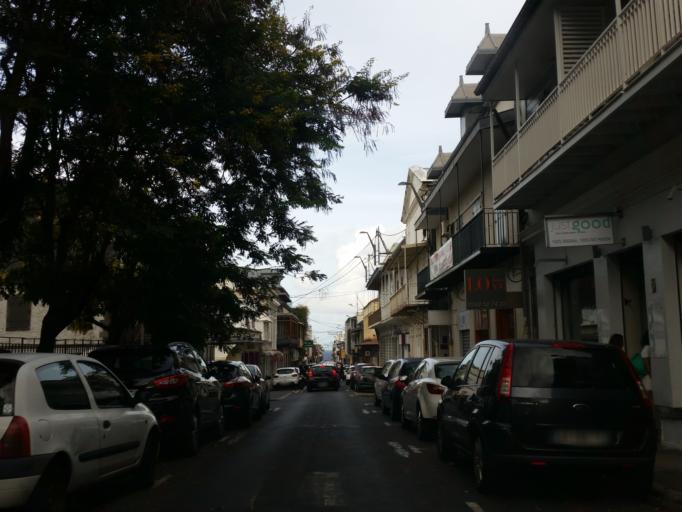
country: RE
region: Reunion
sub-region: Reunion
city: Saint-Denis
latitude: -20.8774
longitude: 55.4488
